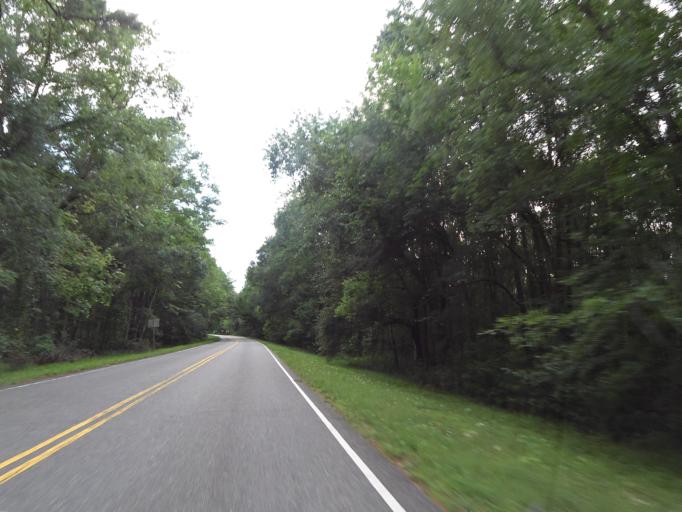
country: US
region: Florida
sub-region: Duval County
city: Jacksonville
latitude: 30.3435
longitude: -81.7787
